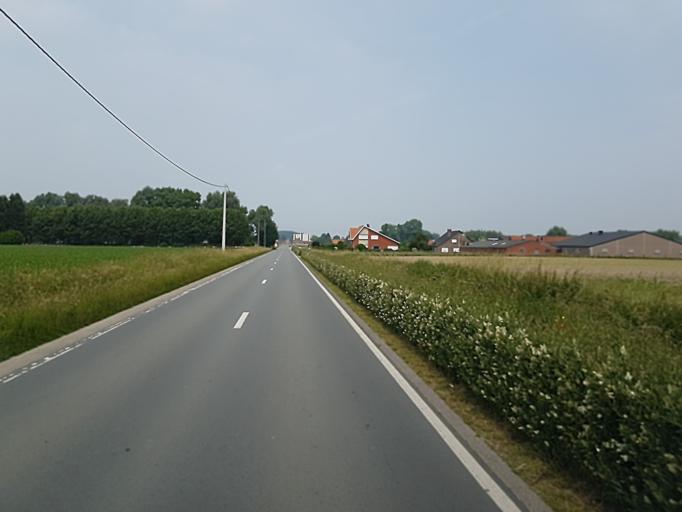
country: BE
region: Flanders
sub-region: Provincie West-Vlaanderen
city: Ardooie
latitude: 50.9513
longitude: 3.2001
